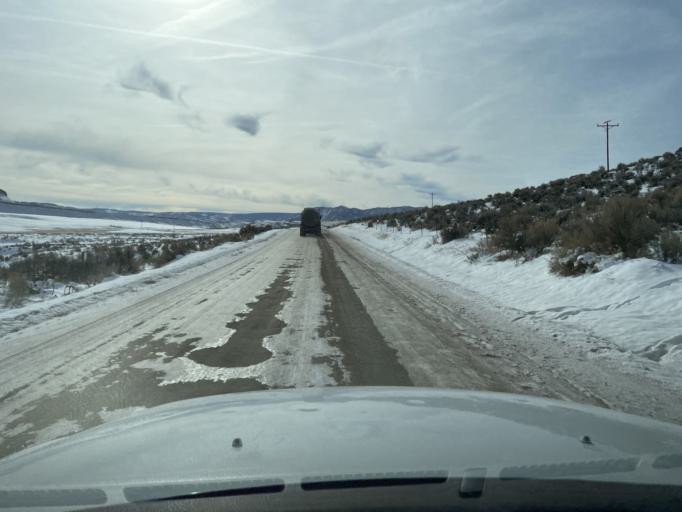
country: US
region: Colorado
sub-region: Moffat County
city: Craig
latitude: 40.3287
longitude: -107.6871
